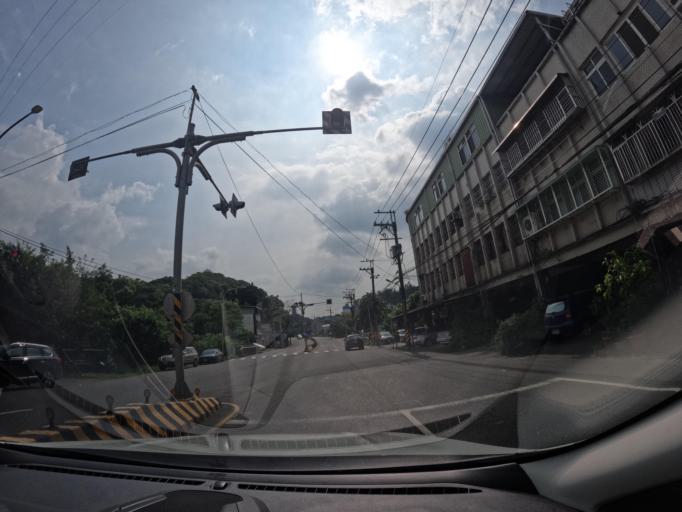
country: TW
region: Taiwan
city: Daxi
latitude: 24.9036
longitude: 121.3529
